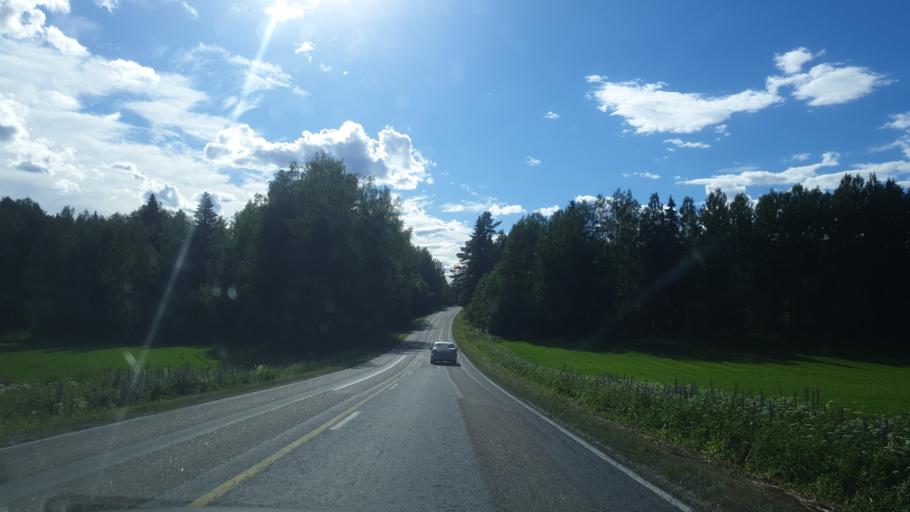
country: FI
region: Southern Savonia
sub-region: Mikkeli
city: Pertunmaa
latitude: 61.5227
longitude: 26.5568
